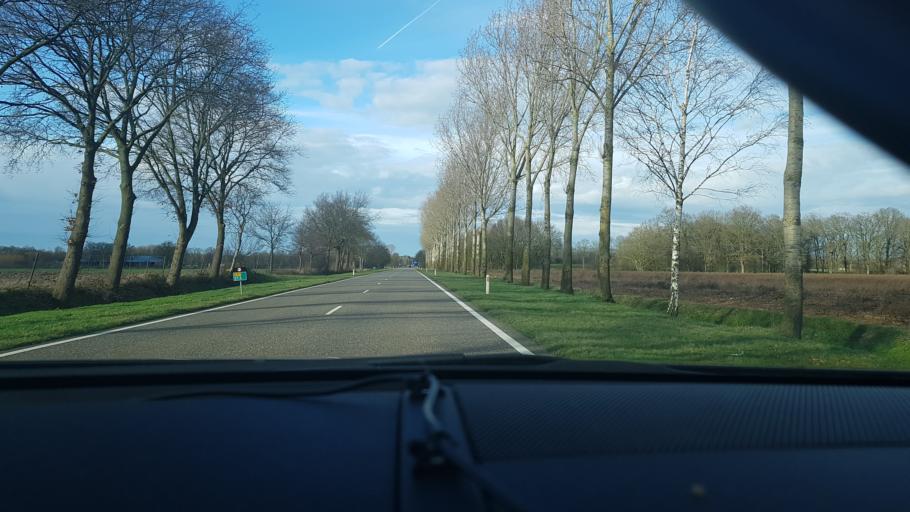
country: NL
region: Limburg
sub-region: Gemeente Peel en Maas
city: Maasbree
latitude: 51.3446
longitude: 6.0232
